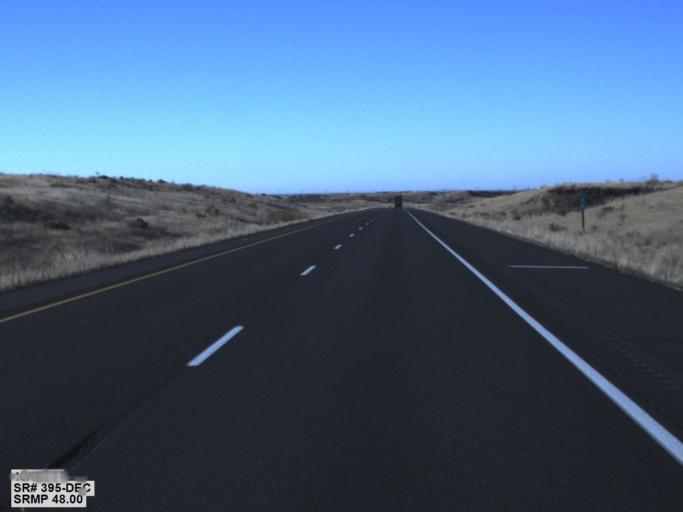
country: US
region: Washington
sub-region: Franklin County
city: Connell
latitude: 46.5894
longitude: -118.9630
